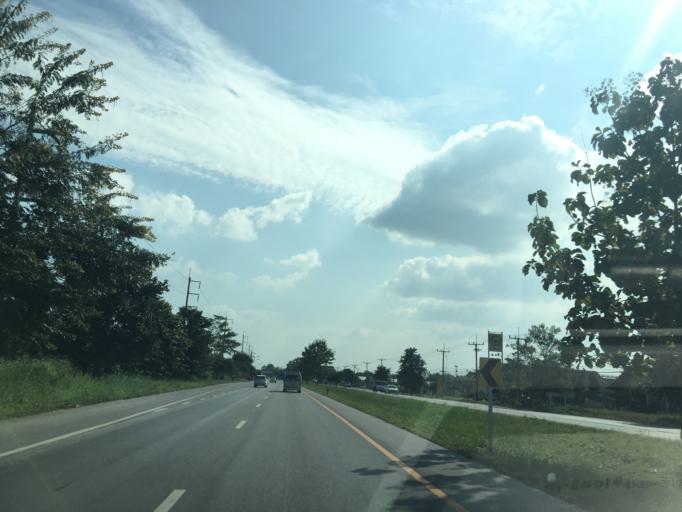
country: TH
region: Chiang Rai
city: Mae Lao
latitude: 19.7260
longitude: 99.7165
